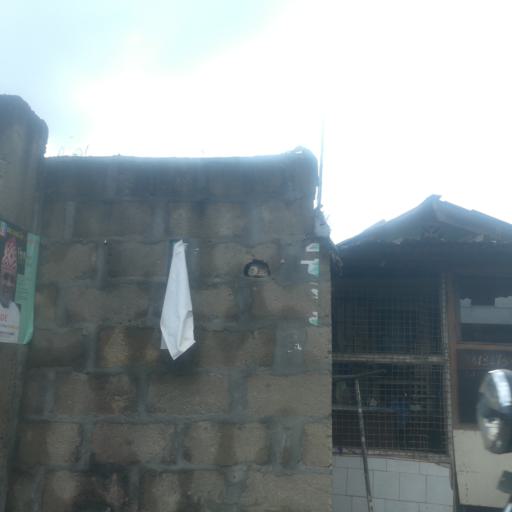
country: NG
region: Lagos
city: Ojota
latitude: 6.6044
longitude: 3.3960
